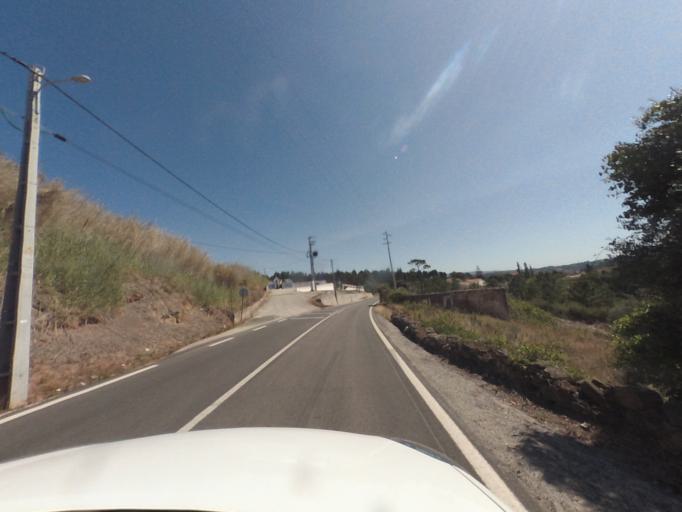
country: PT
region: Leiria
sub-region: Alcobaca
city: Alcobaca
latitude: 39.5115
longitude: -8.9742
